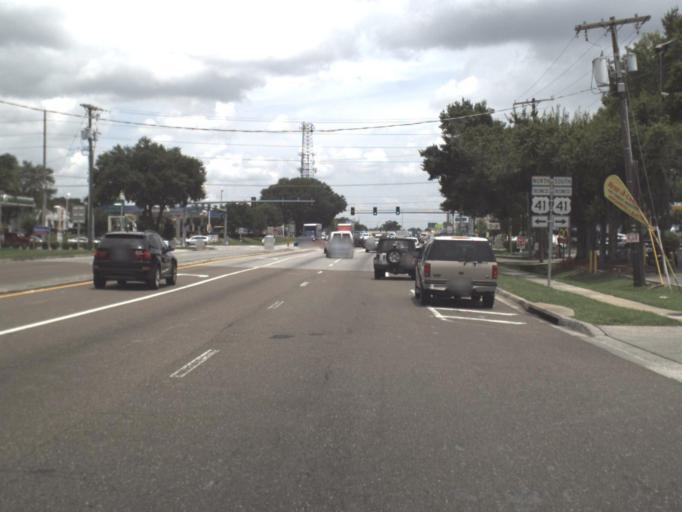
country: US
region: Florida
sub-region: Hillsborough County
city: Lake Magdalene
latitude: 28.0880
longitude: -82.4611
